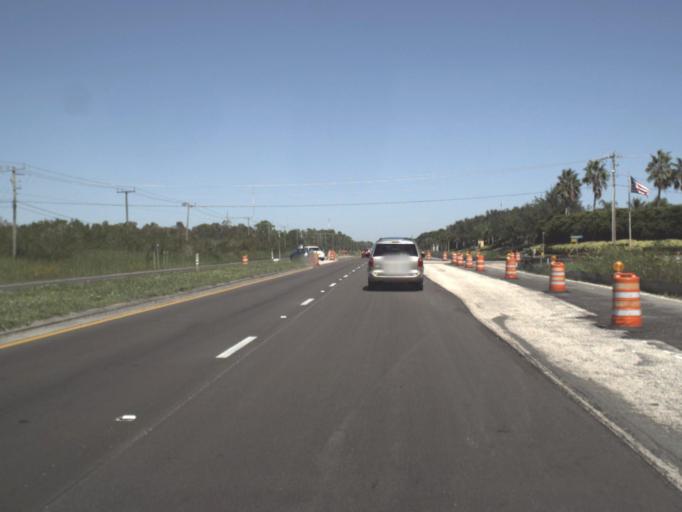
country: US
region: Florida
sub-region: Collier County
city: Lely Resort
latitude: 26.0316
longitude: -81.7005
